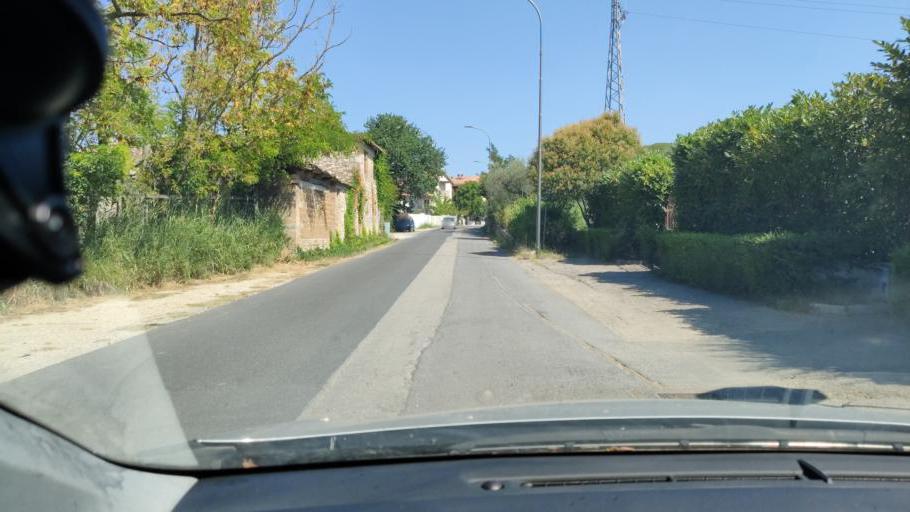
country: IT
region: Umbria
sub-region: Provincia di Terni
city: Fornole
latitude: 42.5376
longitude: 12.4542
